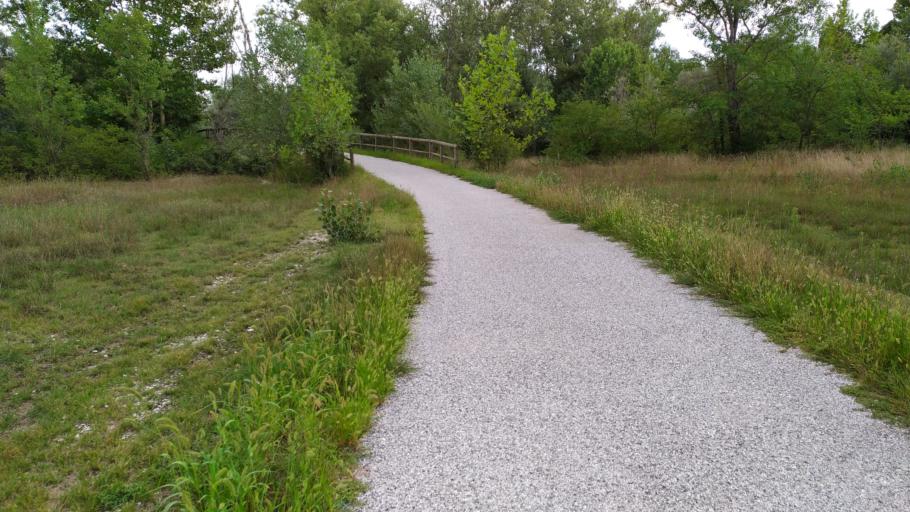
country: IT
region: Veneto
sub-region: Provincia di Padova
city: Grantorto
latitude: 45.6026
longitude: 11.7528
